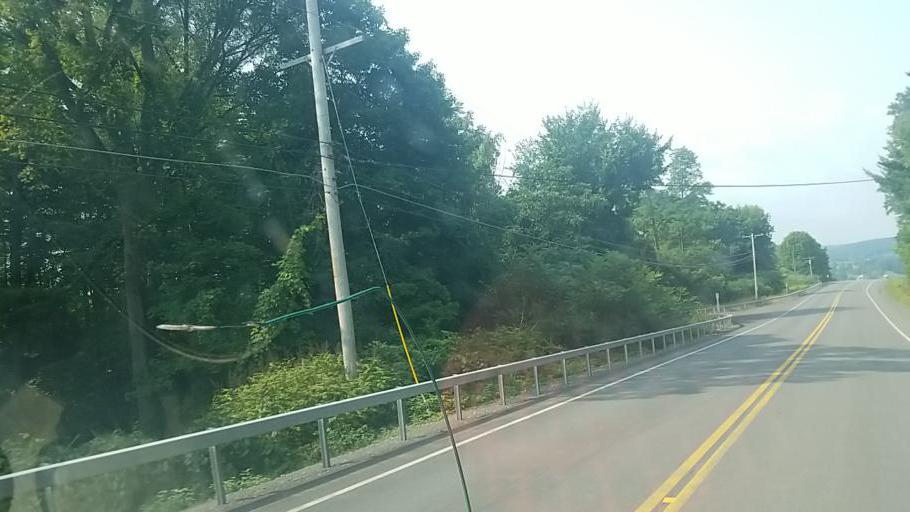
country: US
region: New York
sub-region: Fulton County
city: Johnstown
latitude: 42.9949
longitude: -74.4205
